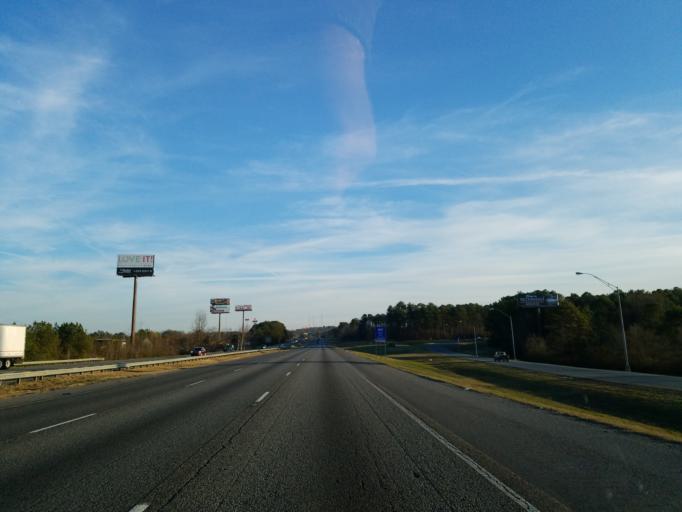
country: US
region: Georgia
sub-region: Gordon County
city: Calhoun
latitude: 34.5679
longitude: -84.9445
